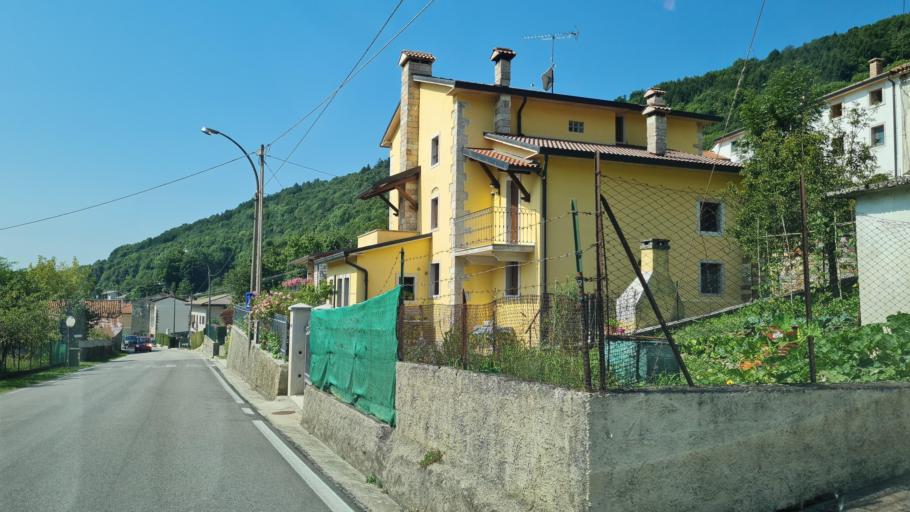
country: IT
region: Veneto
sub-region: Provincia di Vicenza
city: Conco
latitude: 45.7952
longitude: 11.6113
